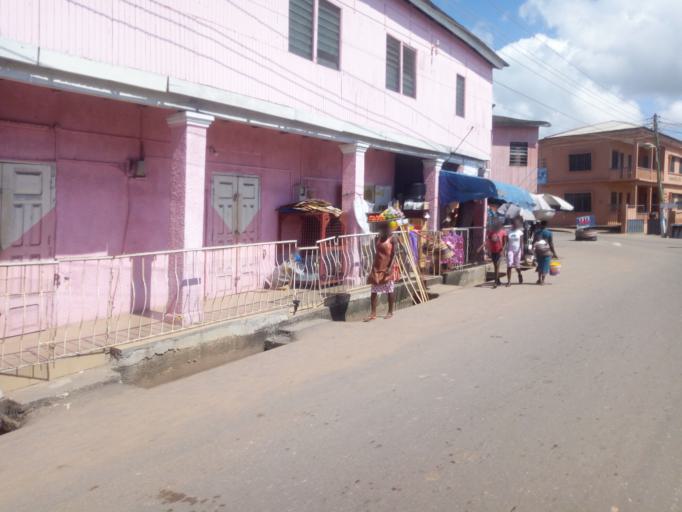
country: GH
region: Central
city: Elmina
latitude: 5.0878
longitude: -1.3488
